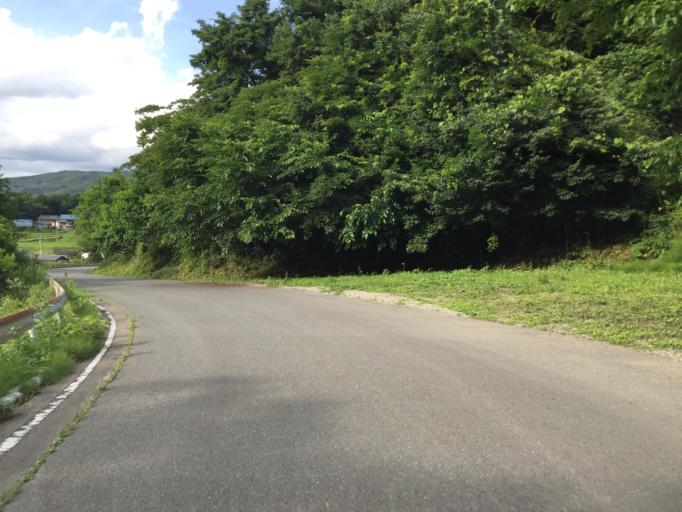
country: JP
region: Fukushima
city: Fukushima-shi
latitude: 37.6884
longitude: 140.5256
